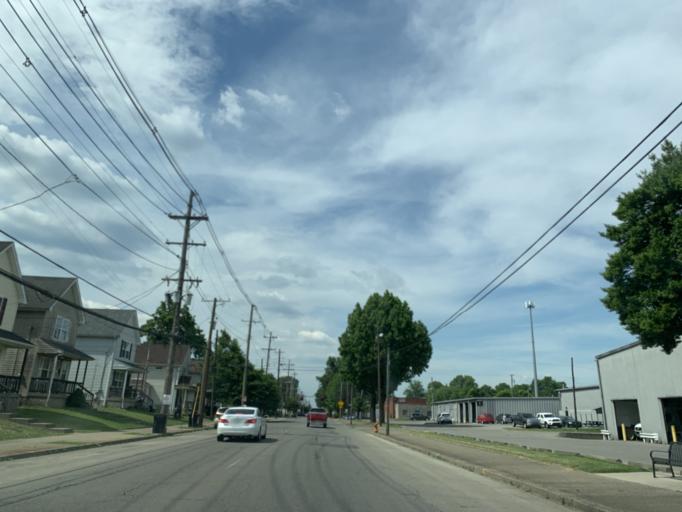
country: US
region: Kentucky
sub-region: Jefferson County
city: Louisville
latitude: 38.2497
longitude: -85.7763
